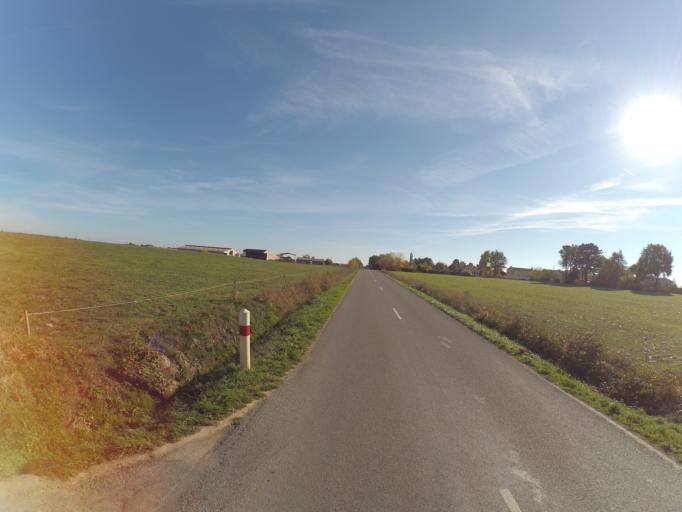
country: FR
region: Pays de la Loire
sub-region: Departement de la Loire-Atlantique
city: Saint-Lumine-de-Clisson
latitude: 47.0743
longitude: -1.3267
